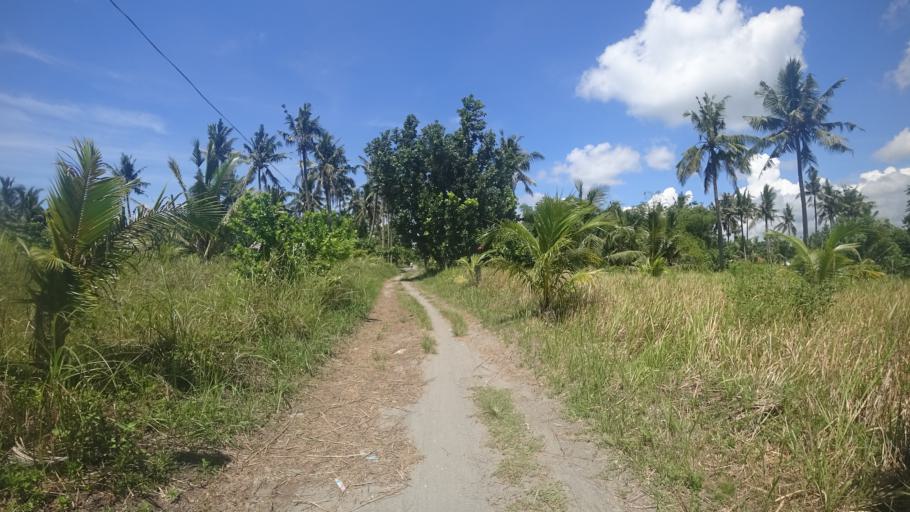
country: PH
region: Eastern Visayas
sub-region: Province of Leyte
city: Mayorga
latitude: 10.8902
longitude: 125.0132
